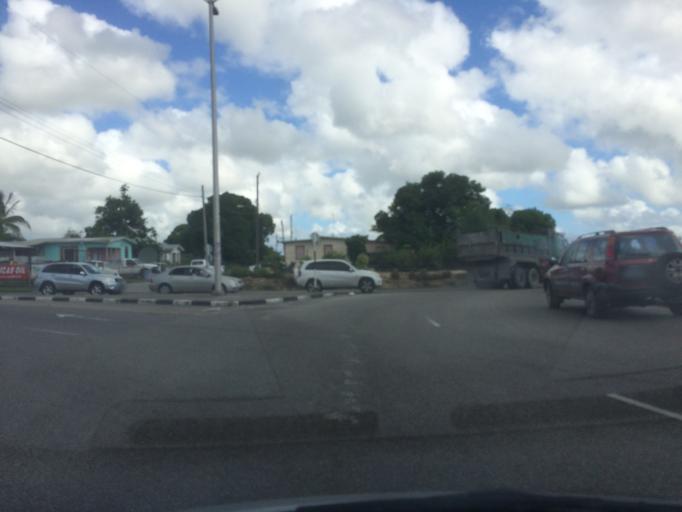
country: BB
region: Saint Michael
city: Bridgetown
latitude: 13.1271
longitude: -59.5955
